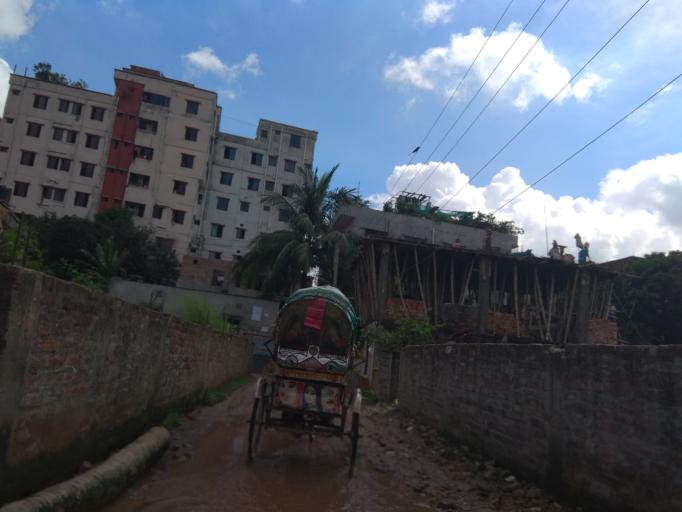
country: BD
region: Dhaka
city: Tungi
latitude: 23.8161
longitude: 90.3898
